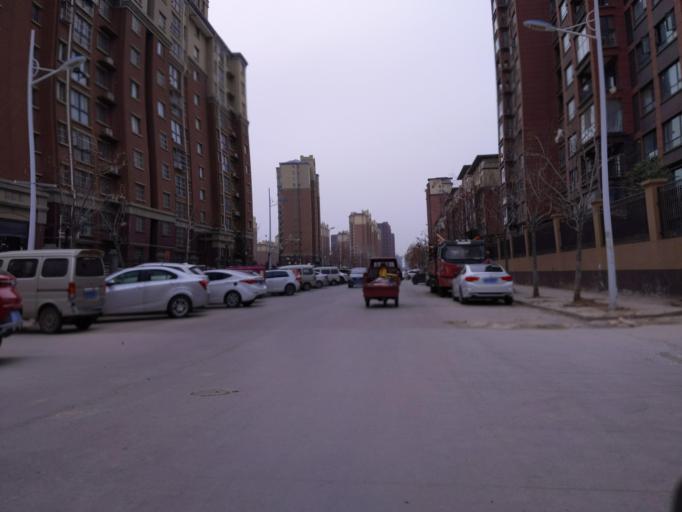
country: CN
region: Henan Sheng
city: Zhongyuanlu
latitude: 35.7419
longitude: 115.0787
